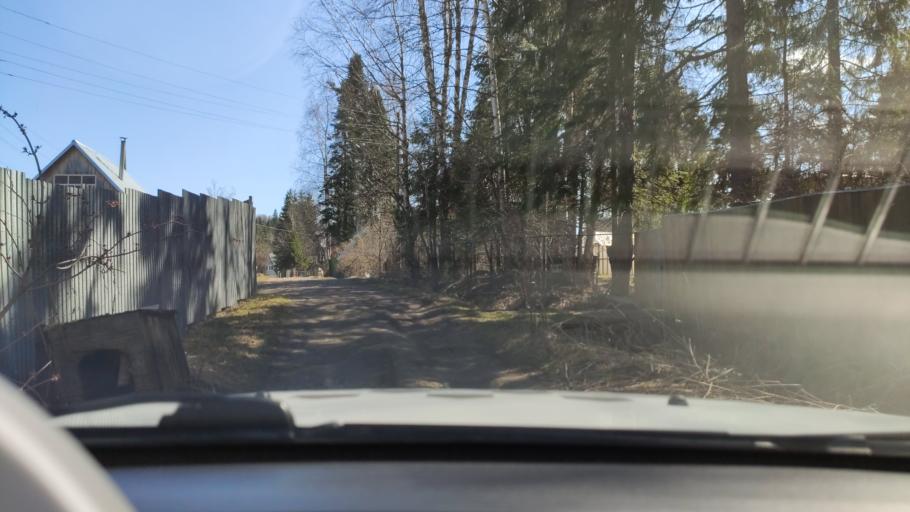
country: RU
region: Perm
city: Novyye Lyady
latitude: 58.0488
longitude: 56.6511
